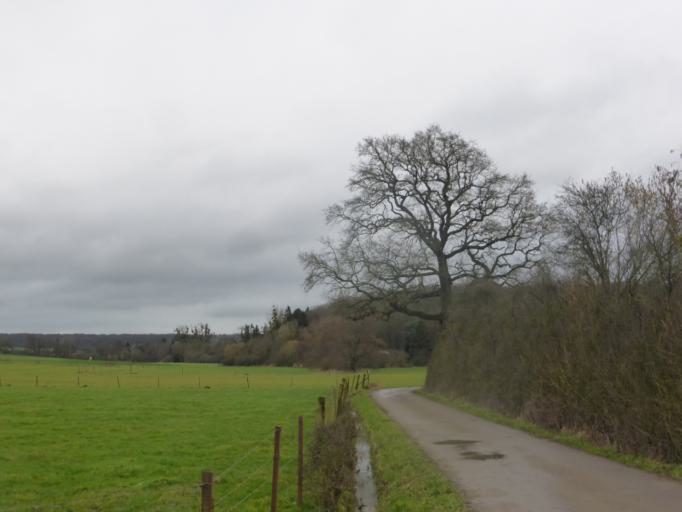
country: LU
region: Luxembourg
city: Bergem
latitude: 49.5356
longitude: 6.0498
